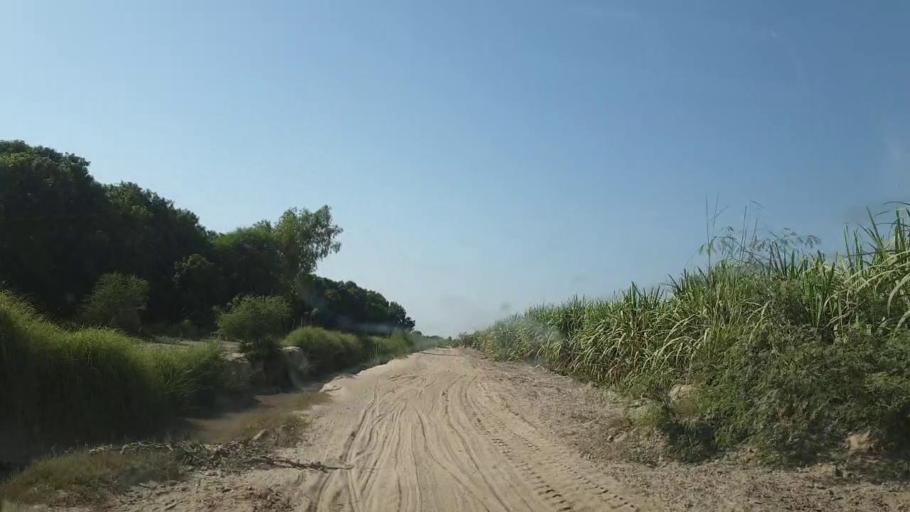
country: PK
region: Sindh
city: Tando Jam
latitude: 25.3162
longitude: 68.6052
